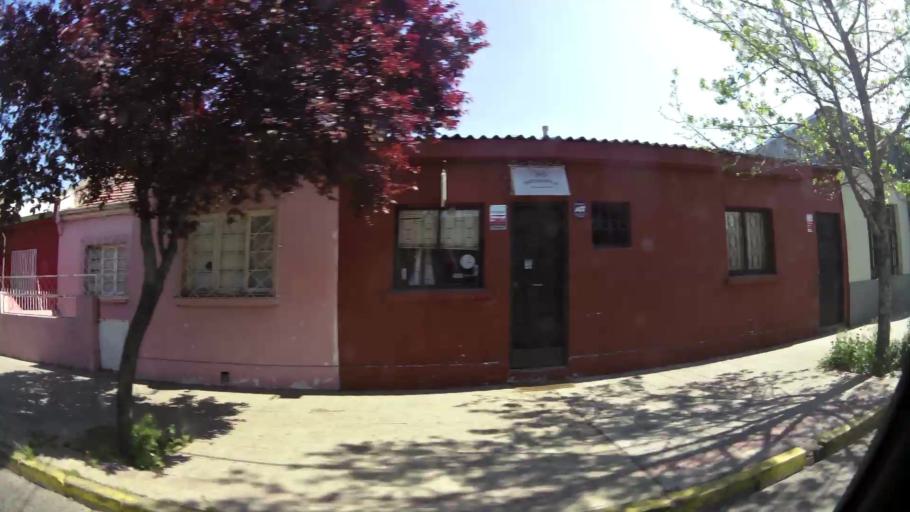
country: CL
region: Santiago Metropolitan
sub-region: Provincia de Santiago
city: Santiago
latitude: -33.4614
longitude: -70.6352
